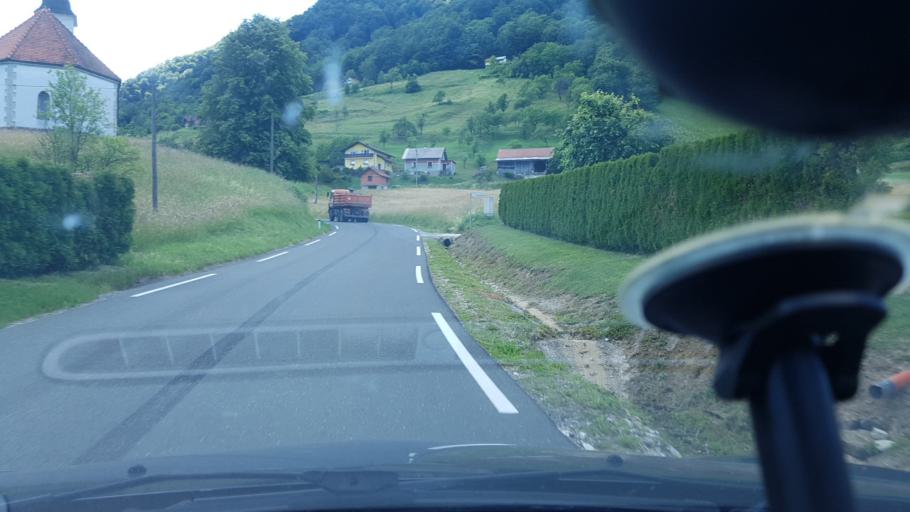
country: SI
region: Zetale
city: Zetale
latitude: 46.2697
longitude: 15.7808
